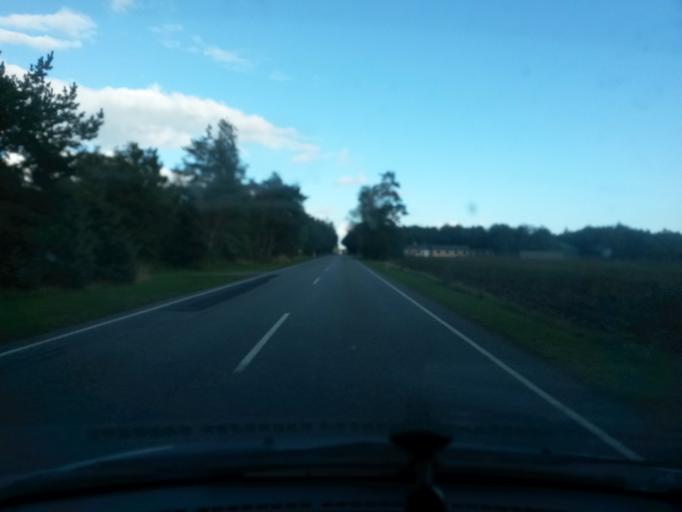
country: DK
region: Central Jutland
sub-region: Viborg Kommune
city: Karup
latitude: 56.3084
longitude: 9.2001
